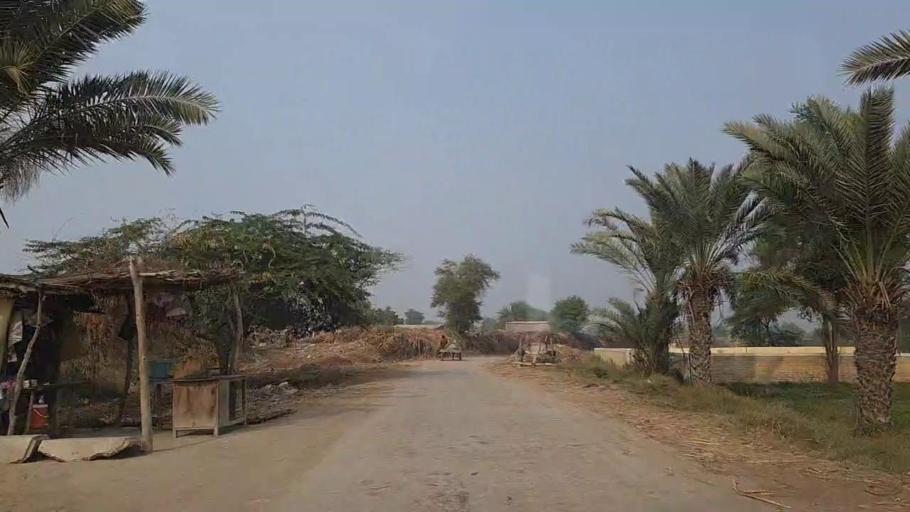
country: PK
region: Sindh
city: Sanghar
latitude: 26.0852
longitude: 68.8964
